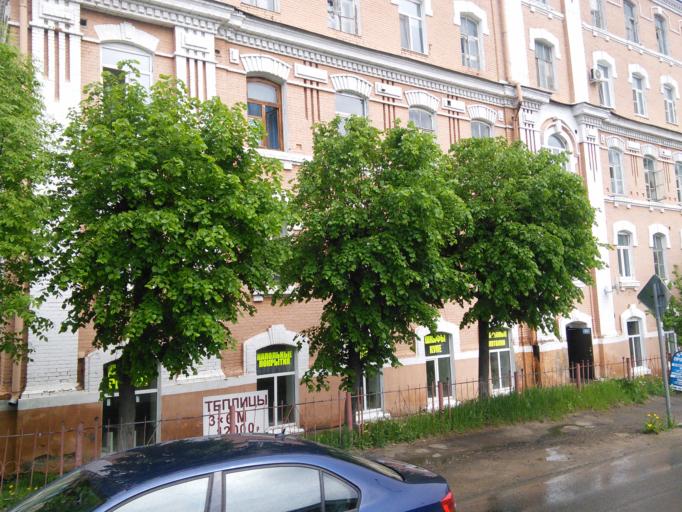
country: RU
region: Moskovskaya
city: Serpukhov
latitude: 54.9281
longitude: 37.3696
